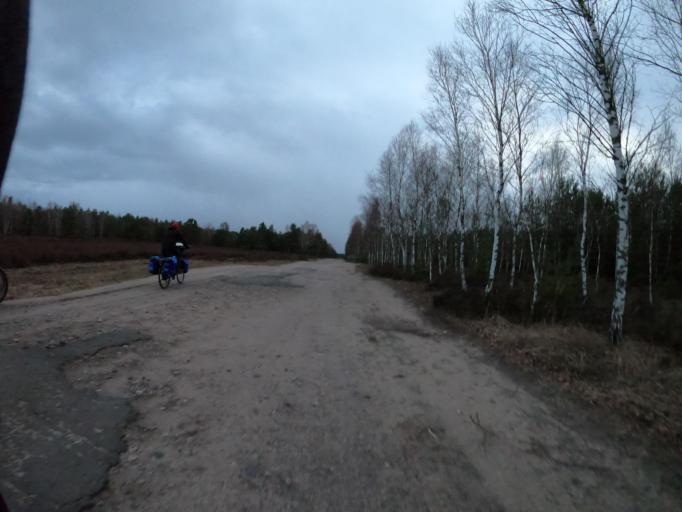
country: PL
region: West Pomeranian Voivodeship
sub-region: Powiat szczecinecki
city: Borne Sulinowo
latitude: 53.5251
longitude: 16.5686
